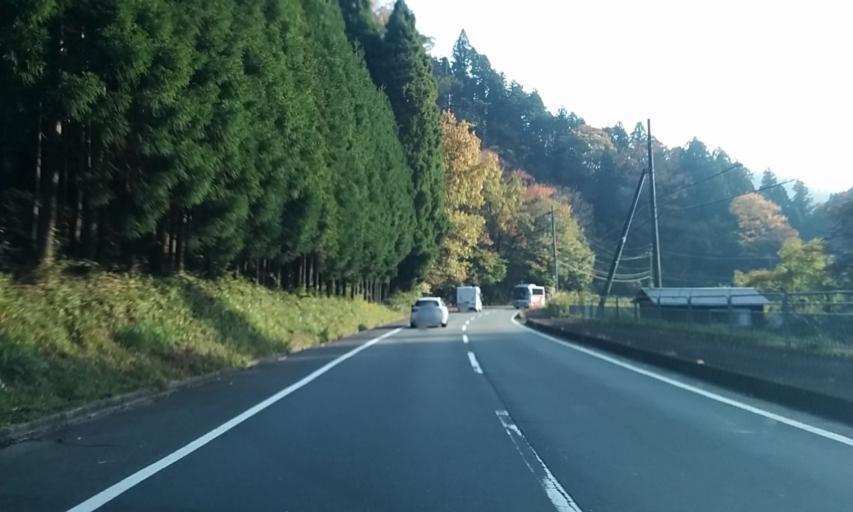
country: JP
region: Kyoto
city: Kameoka
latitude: 35.1598
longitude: 135.5151
